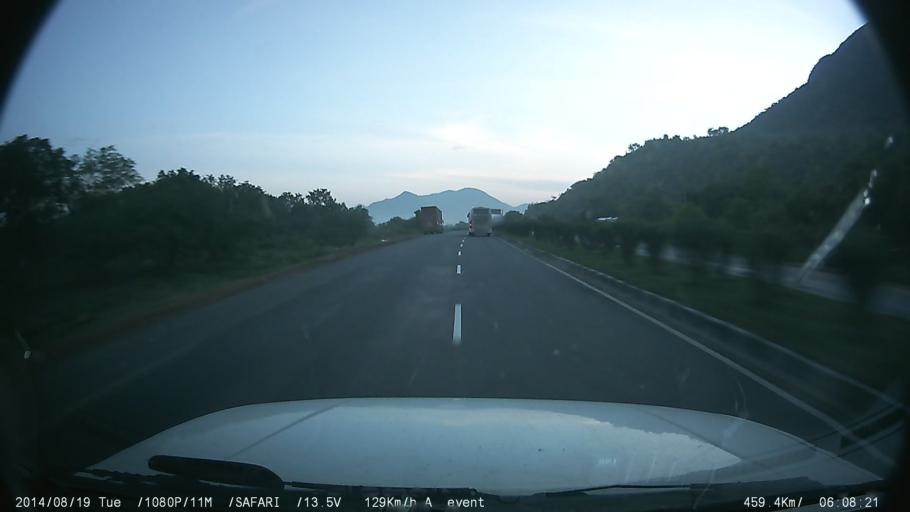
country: IN
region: Tamil Nadu
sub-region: Salem
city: Omalur
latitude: 11.9156
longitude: 78.0596
